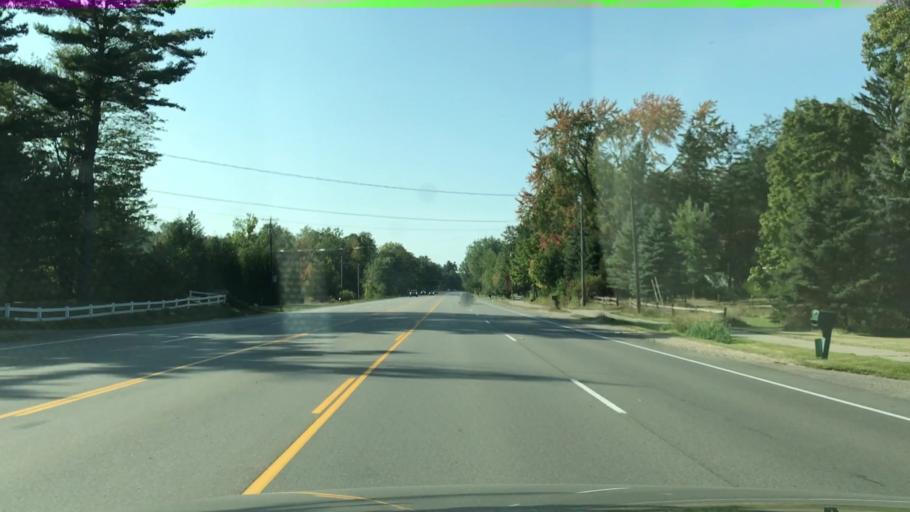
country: US
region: Michigan
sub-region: Kent County
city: Forest Hills
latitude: 42.9263
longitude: -85.5126
